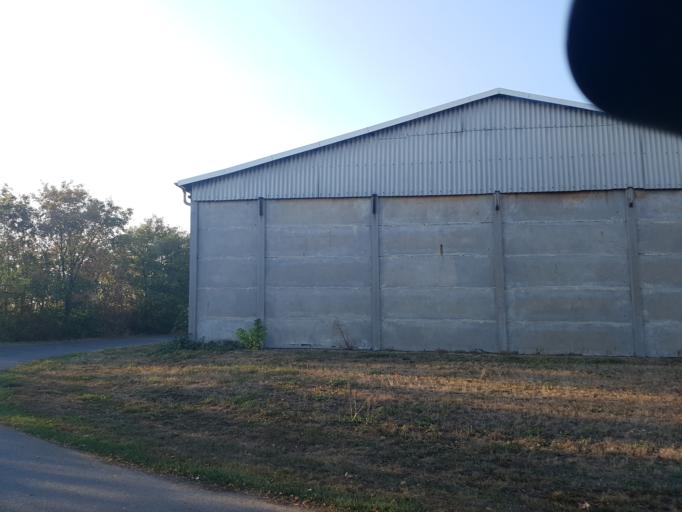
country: DE
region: Brandenburg
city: Muhlberg
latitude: 51.4984
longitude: 13.2835
